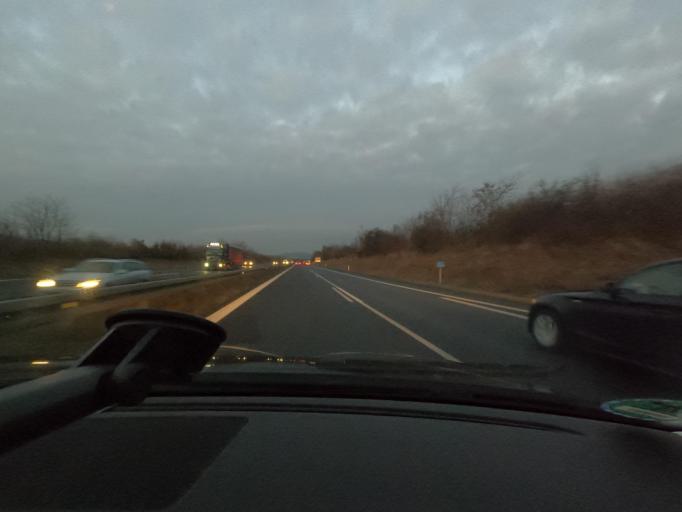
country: DE
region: Bavaria
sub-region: Upper Franconia
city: Bad Staffelstein
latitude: 50.1117
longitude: 11.0150
